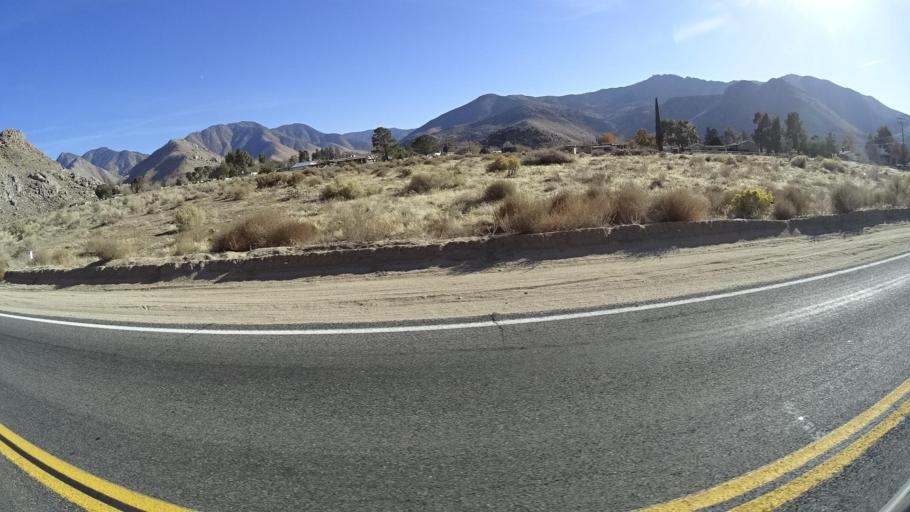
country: US
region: California
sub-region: Kern County
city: Weldon
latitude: 35.6936
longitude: -118.2225
